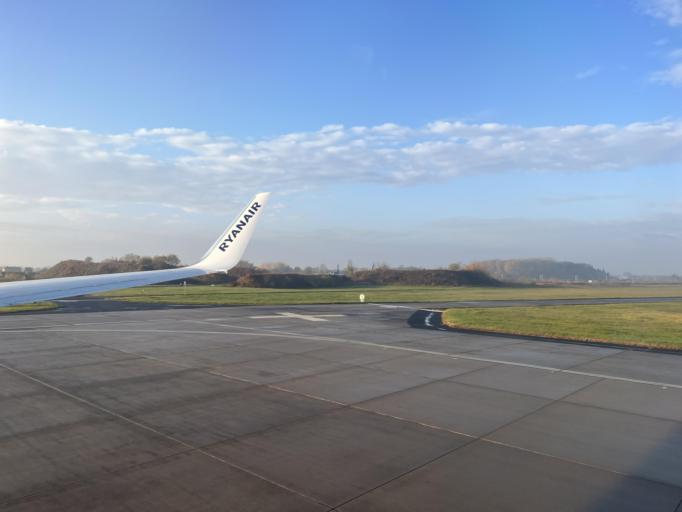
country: PL
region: Silesian Voivodeship
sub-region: Powiat tarnogorski
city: Ozarowice
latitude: 50.4726
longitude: 19.0664
